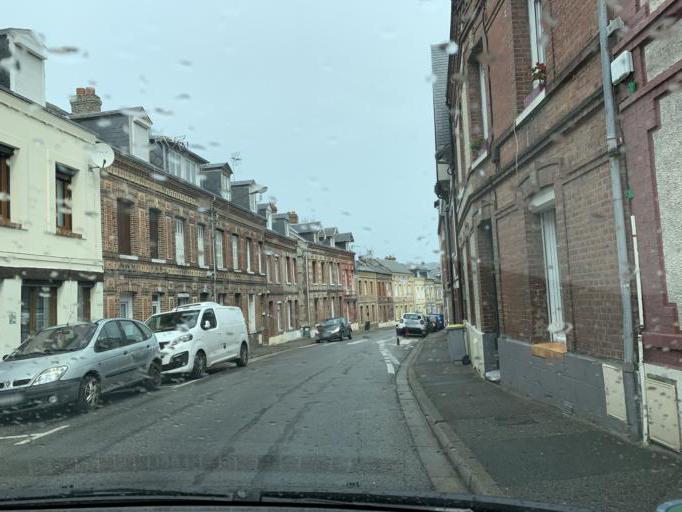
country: FR
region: Haute-Normandie
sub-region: Departement de la Seine-Maritime
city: Fecamp
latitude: 49.7564
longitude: 0.3626
